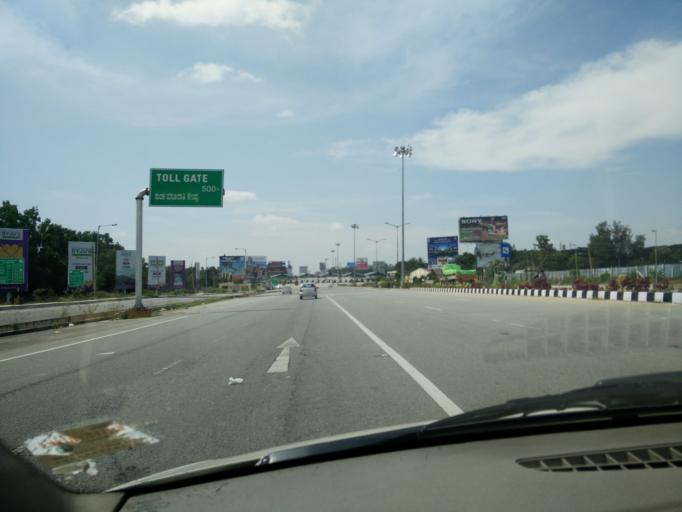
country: IN
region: Karnataka
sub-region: Bangalore Rural
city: Devanhalli
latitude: 13.1962
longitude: 77.6540
